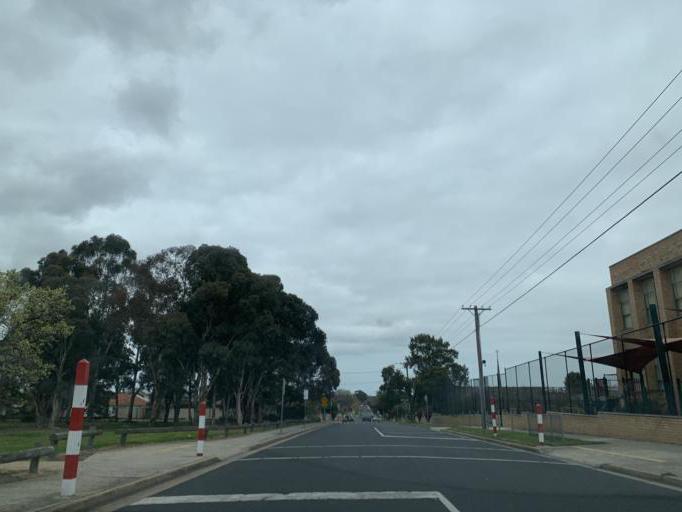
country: AU
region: Victoria
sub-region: Moreland
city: Pascoe Vale
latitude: -37.7302
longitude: 144.9425
